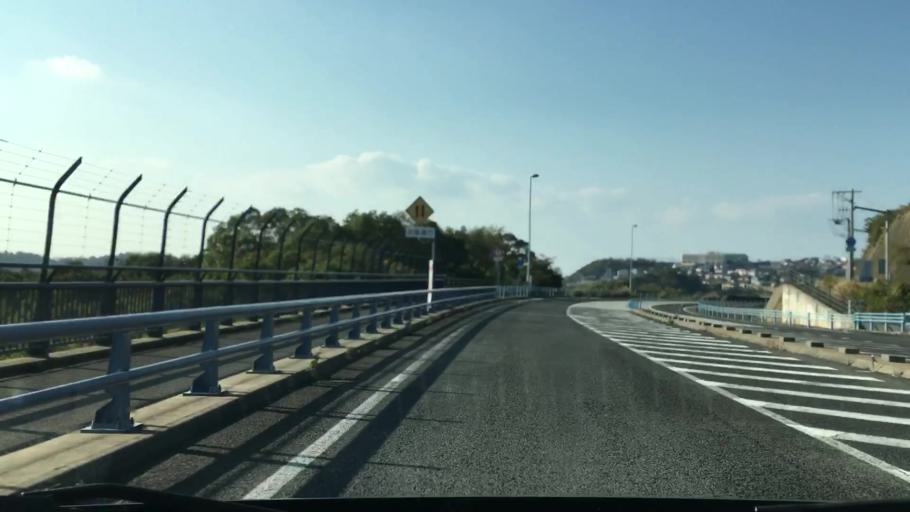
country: JP
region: Nagasaki
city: Nagasaki-shi
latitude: 32.7232
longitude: 129.8443
